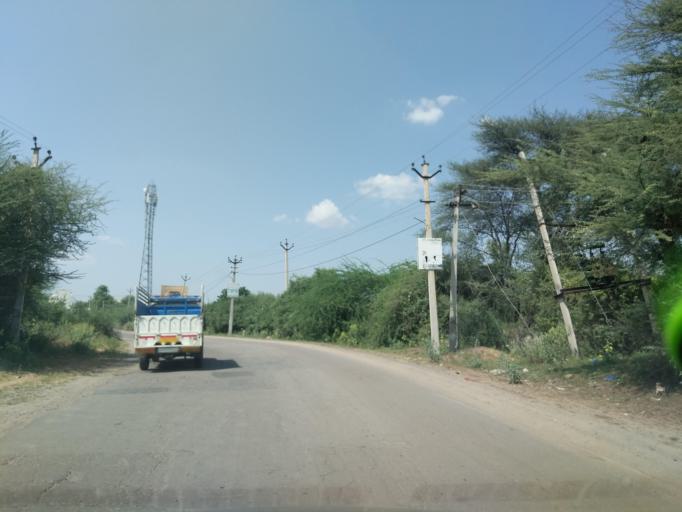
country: IN
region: Rajasthan
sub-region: Jhunjhunun
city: Jhunjhunun
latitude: 28.1553
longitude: 75.3761
